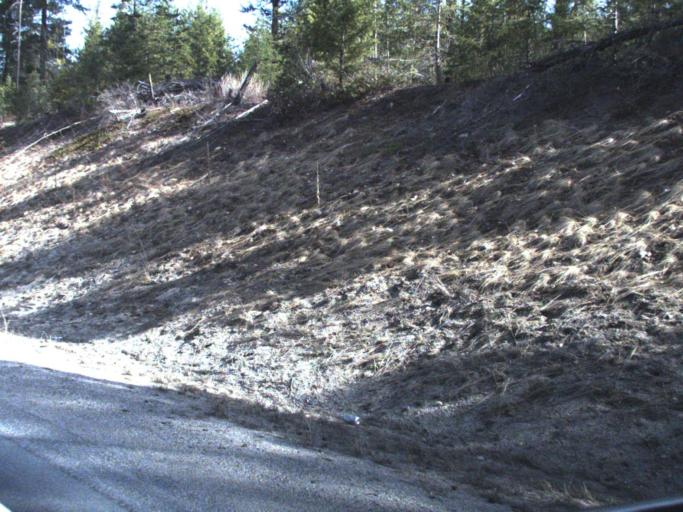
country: US
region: Washington
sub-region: Stevens County
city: Chewelah
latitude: 48.5069
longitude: -117.6736
